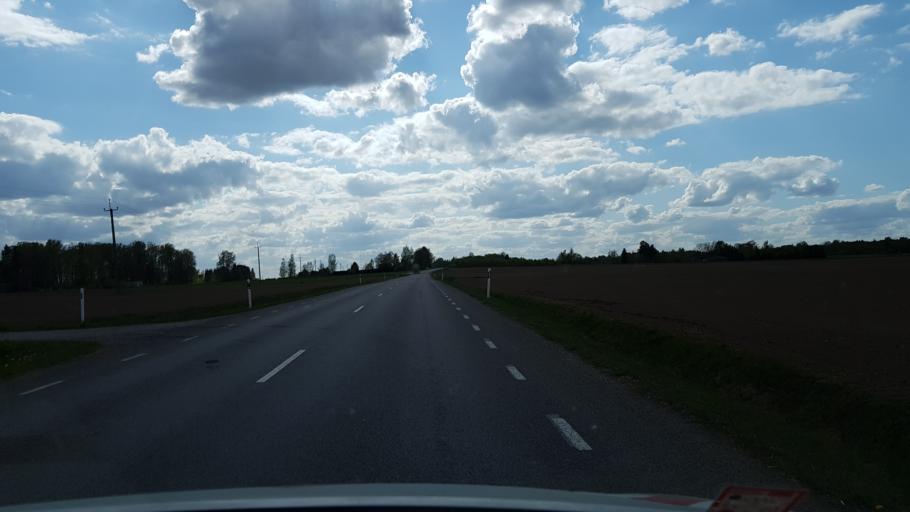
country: EE
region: Tartu
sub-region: Tartu linn
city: Tartu
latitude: 58.3954
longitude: 26.8306
